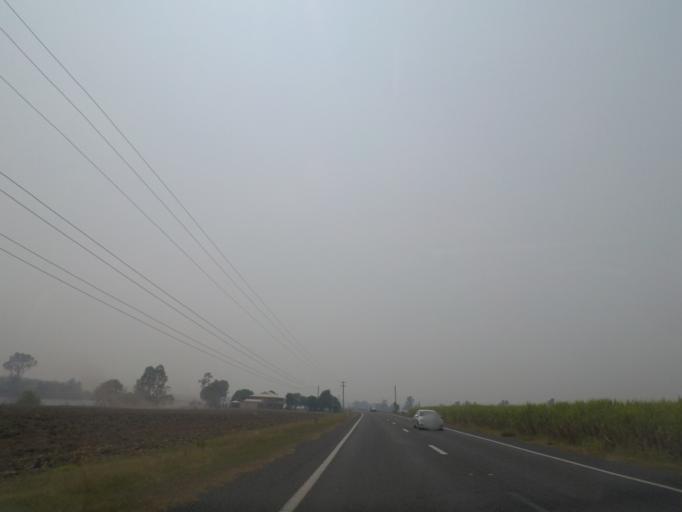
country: AU
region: New South Wales
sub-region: Clarence Valley
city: Maclean
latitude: -29.5651
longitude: 153.1165
